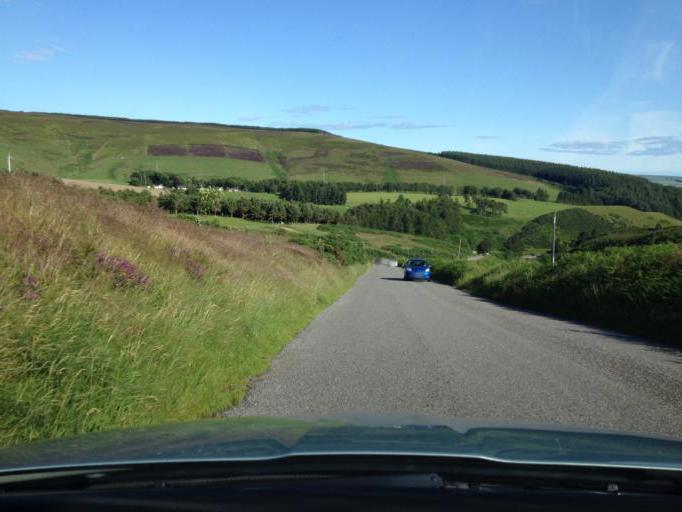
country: GB
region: Scotland
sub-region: Aberdeenshire
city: Laurencekirk
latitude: 56.8981
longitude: -2.5583
